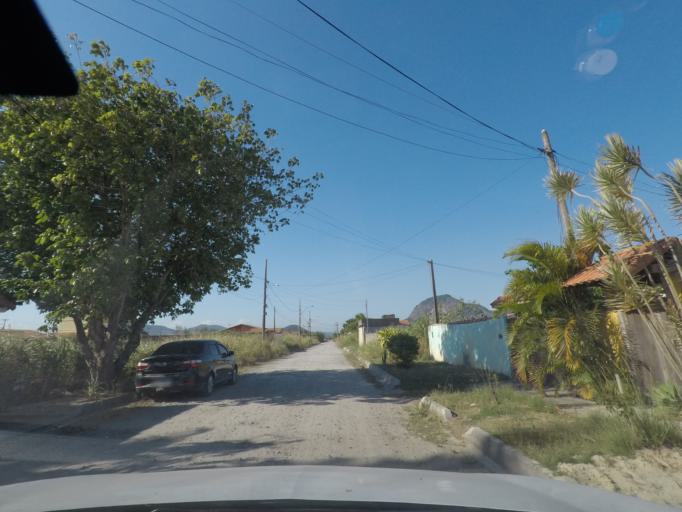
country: BR
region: Rio de Janeiro
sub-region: Marica
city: Marica
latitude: -22.9658
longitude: -42.9253
